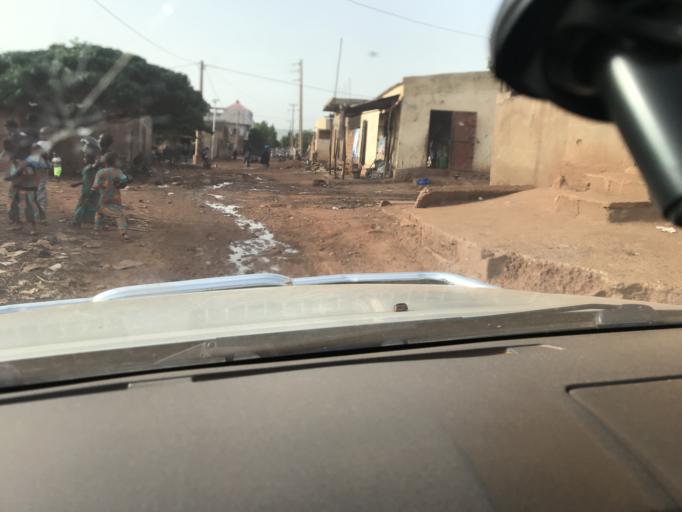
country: ML
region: Bamako
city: Bamako
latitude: 12.5925
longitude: -8.0079
